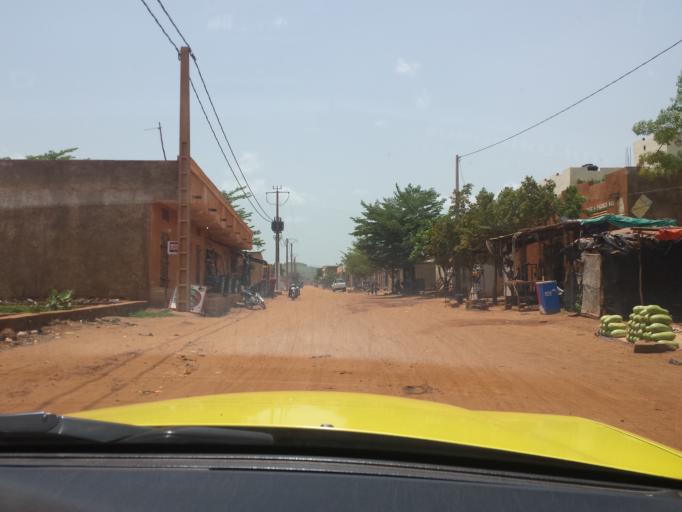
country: ML
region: Bamako
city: Bamako
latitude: 12.6054
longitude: -7.8913
